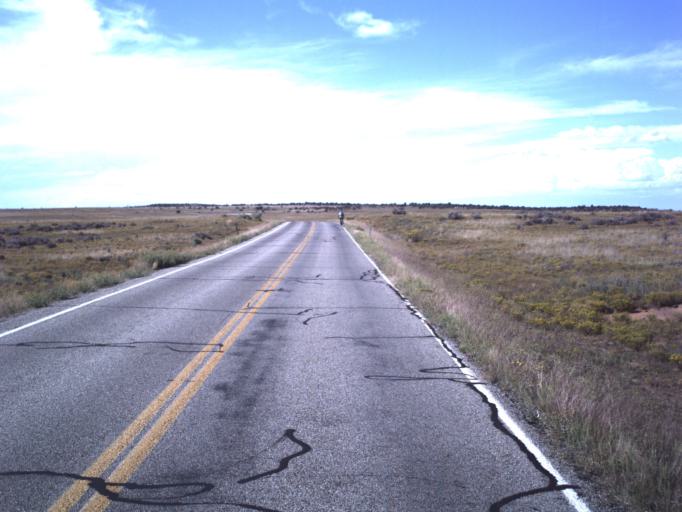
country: US
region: Utah
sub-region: Grand County
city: Moab
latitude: 38.5352
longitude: -109.7539
